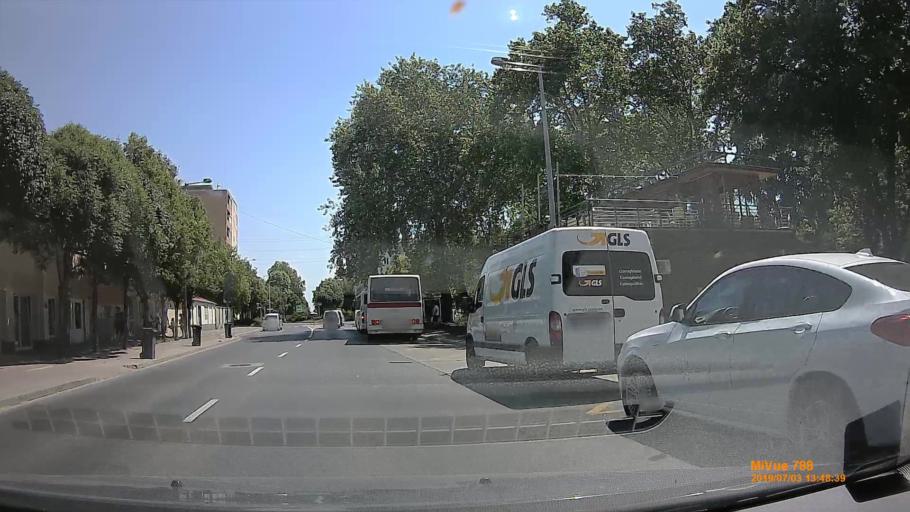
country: HU
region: Gyor-Moson-Sopron
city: Gyor
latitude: 47.6805
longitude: 17.6445
